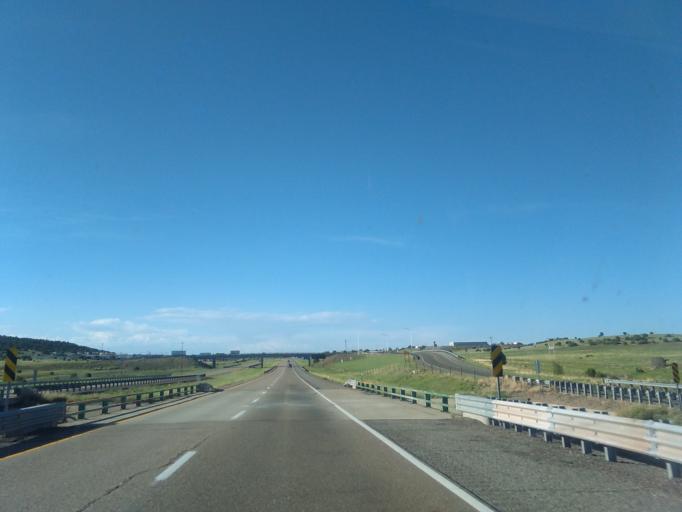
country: US
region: New Mexico
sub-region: San Miguel County
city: Las Vegas
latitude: 35.5539
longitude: -105.2255
